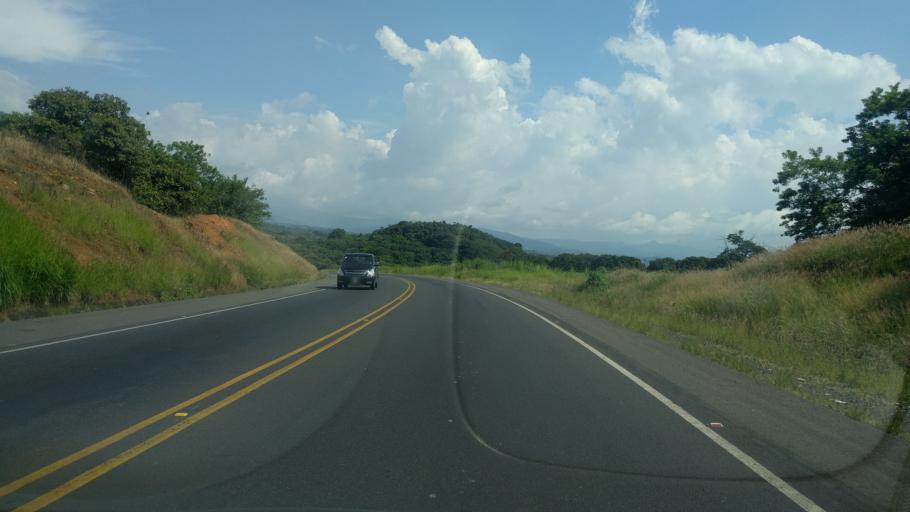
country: CR
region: Alajuela
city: Carrillos
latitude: 10.0104
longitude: -84.3247
